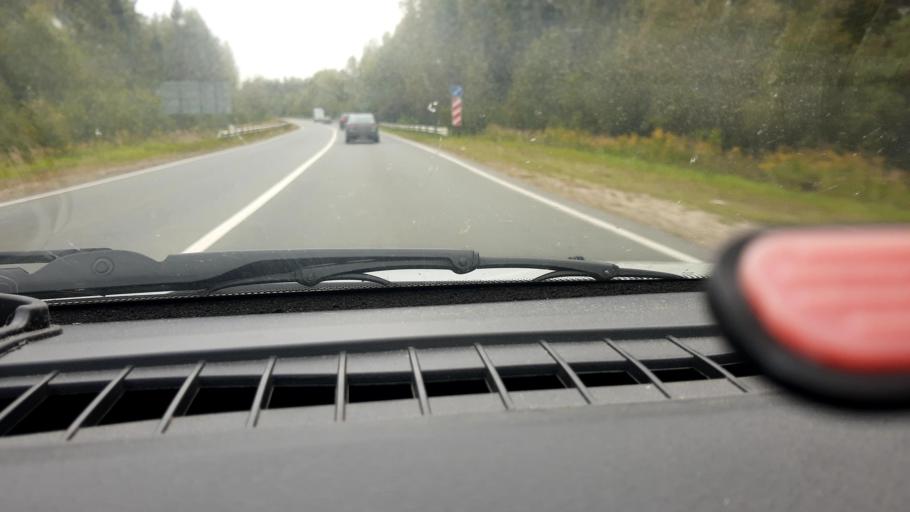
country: RU
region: Nizjnij Novgorod
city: Semenov
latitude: 56.8052
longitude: 44.4626
